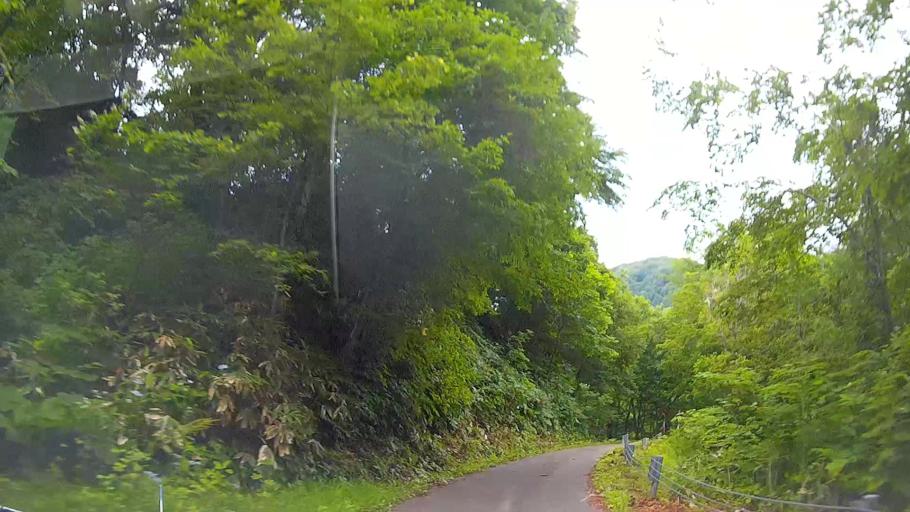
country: JP
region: Hokkaido
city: Nanae
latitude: 42.0462
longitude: 140.4898
